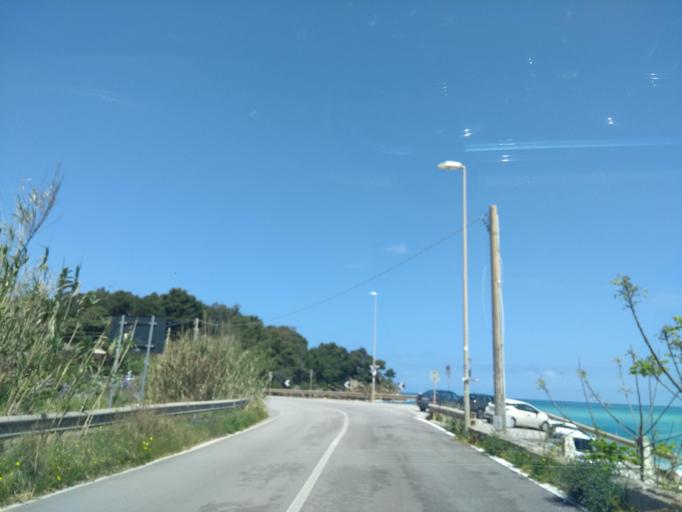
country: IT
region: Sicily
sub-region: Trapani
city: Castellammare del Golfo
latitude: 38.0570
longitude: 12.8390
